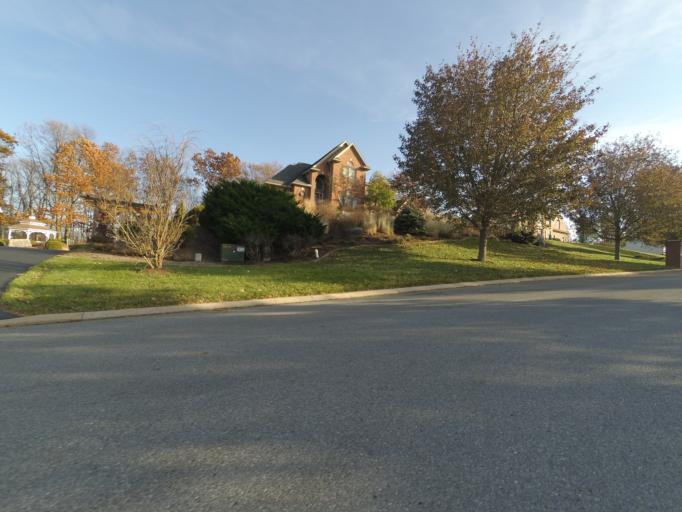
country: US
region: Pennsylvania
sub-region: Centre County
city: Lemont
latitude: 40.7992
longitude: -77.8204
